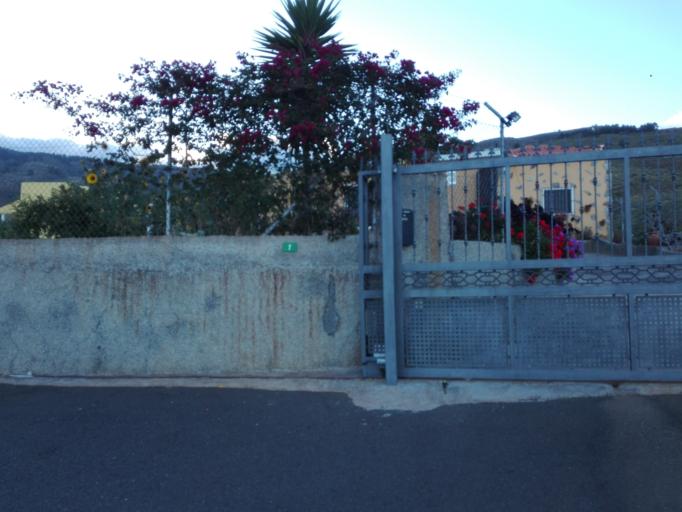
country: ES
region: Canary Islands
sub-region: Provincia de Santa Cruz de Tenerife
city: Candelaria
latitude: 28.4033
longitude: -16.3586
